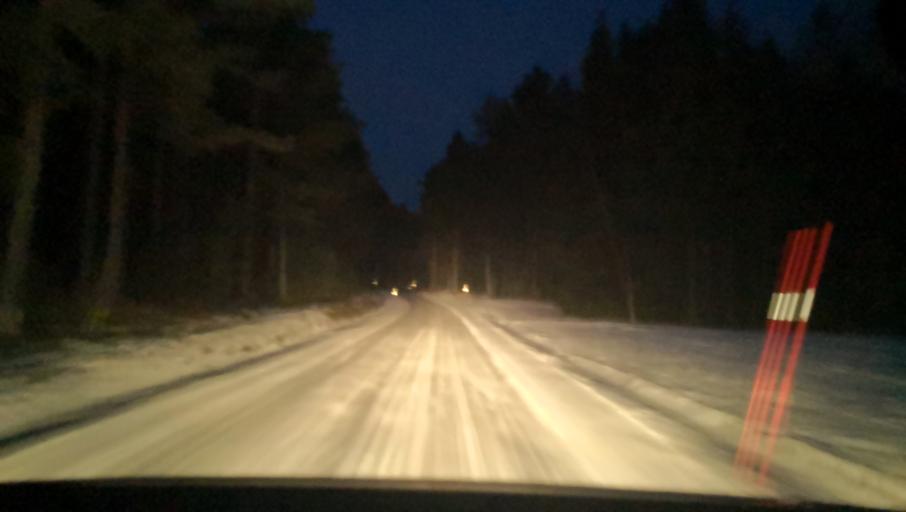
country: SE
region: Uppsala
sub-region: Heby Kommun
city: Tarnsjo
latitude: 60.2754
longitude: 16.7995
